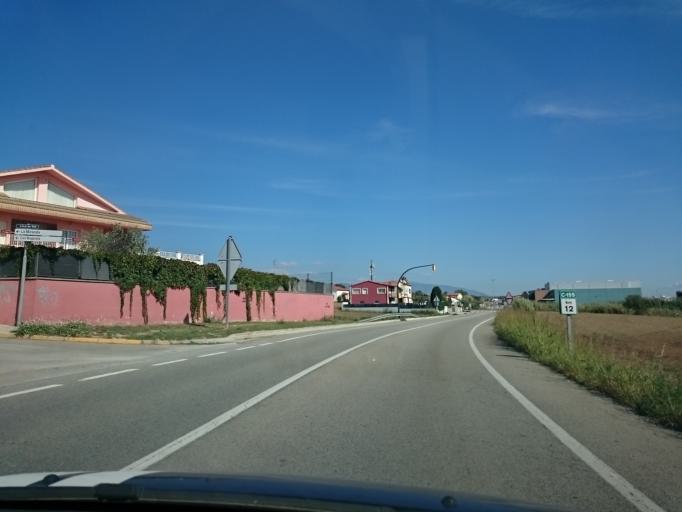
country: ES
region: Catalonia
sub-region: Provincia de Barcelona
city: Parets del Valles
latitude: 41.5771
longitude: 2.2242
